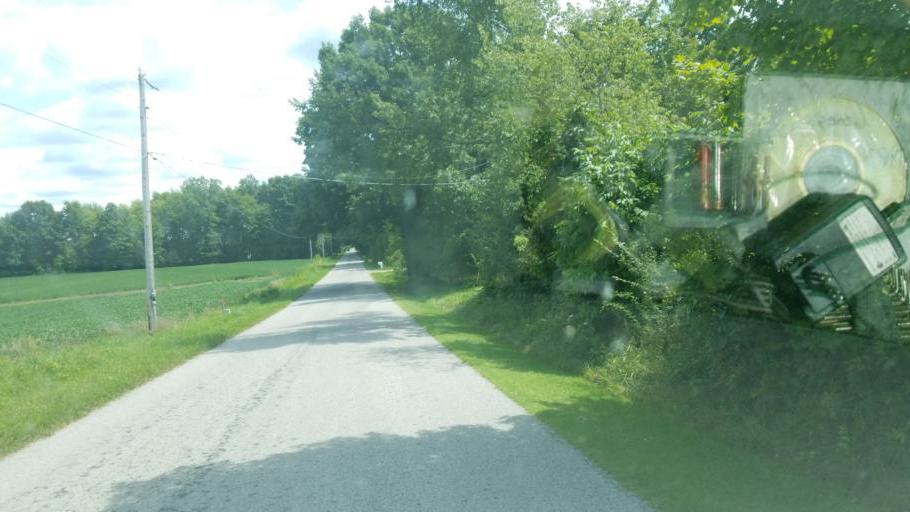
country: US
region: Ohio
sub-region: Delaware County
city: Sunbury
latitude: 40.3379
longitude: -82.8107
